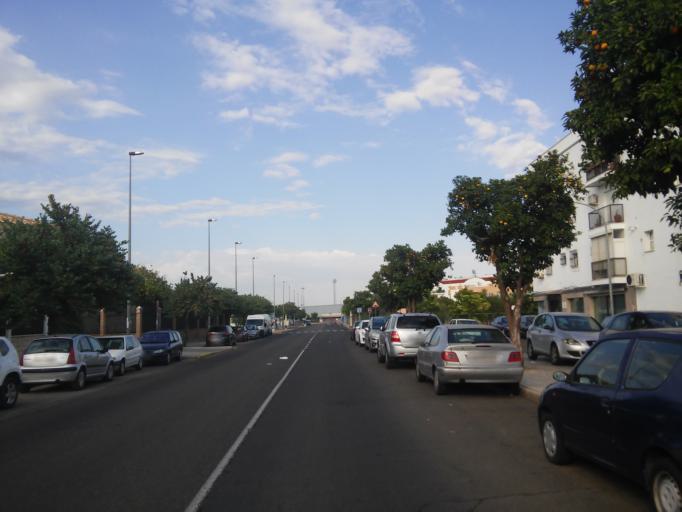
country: ES
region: Andalusia
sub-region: Provincia de Sevilla
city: La Rinconada
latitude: 37.4913
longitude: -5.9431
